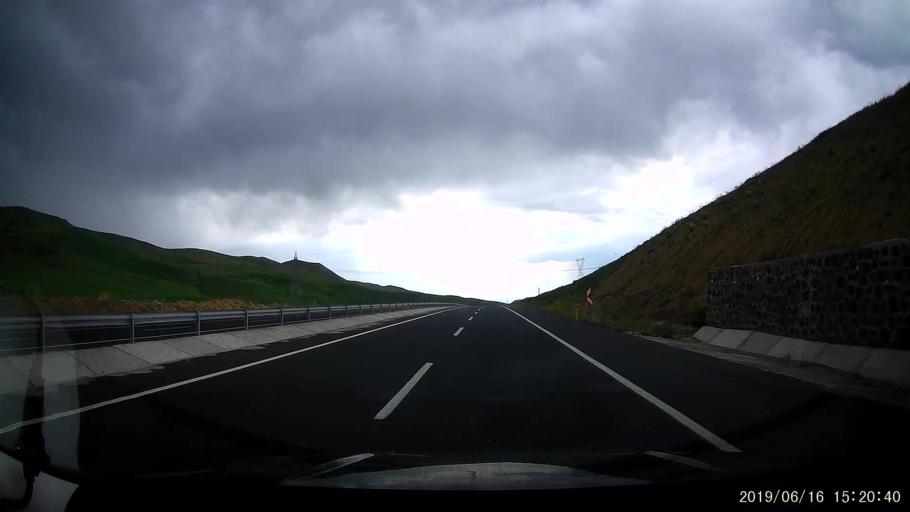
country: TR
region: Erzurum
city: Aras
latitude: 39.9737
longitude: 42.2603
